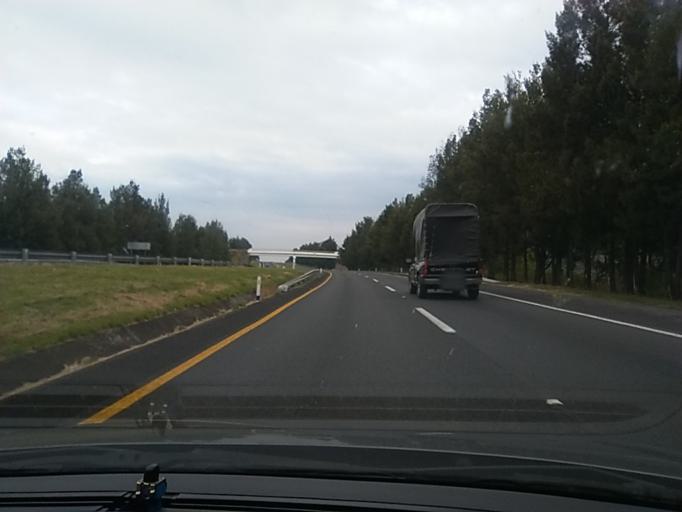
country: MX
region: Michoacan
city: Penjamillo de Degollado
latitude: 20.0835
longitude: -101.9945
